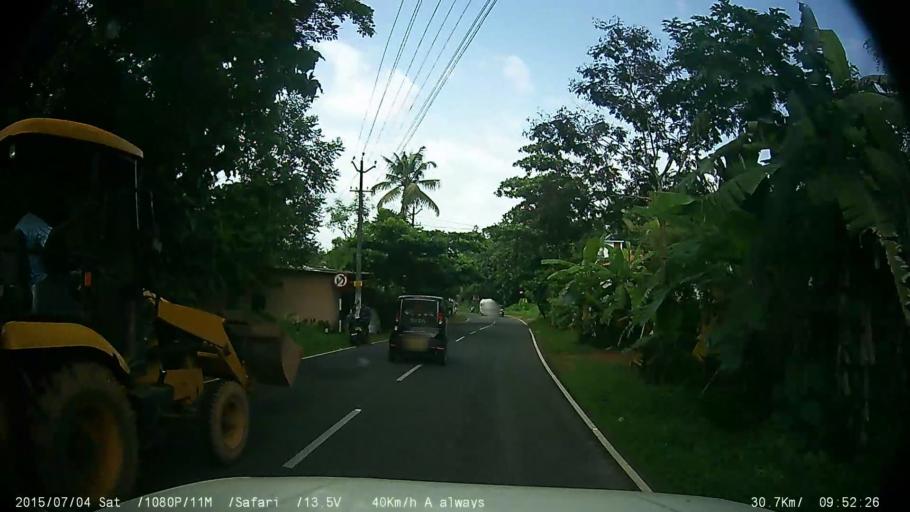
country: IN
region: Kerala
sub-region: Kottayam
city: Kottayam
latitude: 9.5707
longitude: 76.5792
